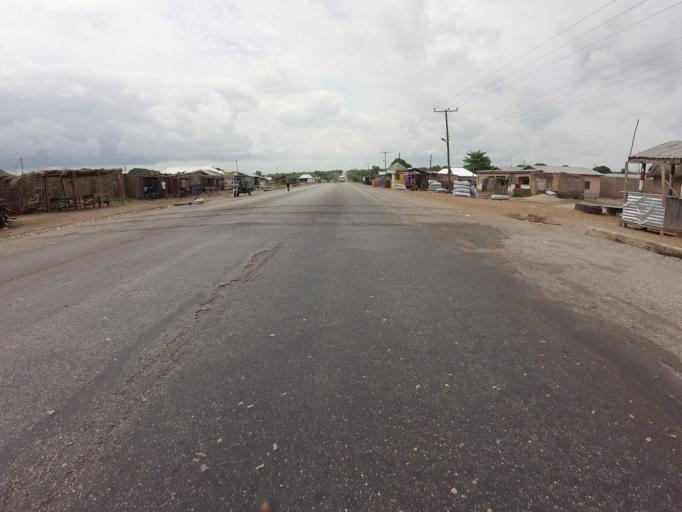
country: GH
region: Brong-Ahafo
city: Kintampo
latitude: 8.6632
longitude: -1.5199
